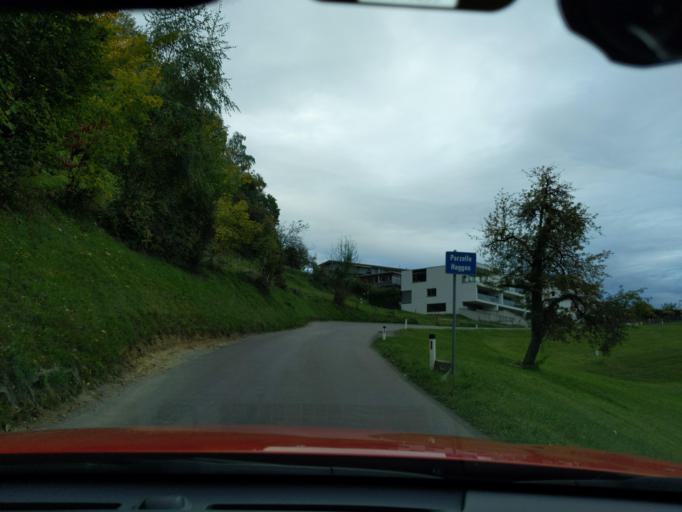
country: AT
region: Vorarlberg
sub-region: Politischer Bezirk Bregenz
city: Lochau
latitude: 47.5176
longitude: 9.7603
